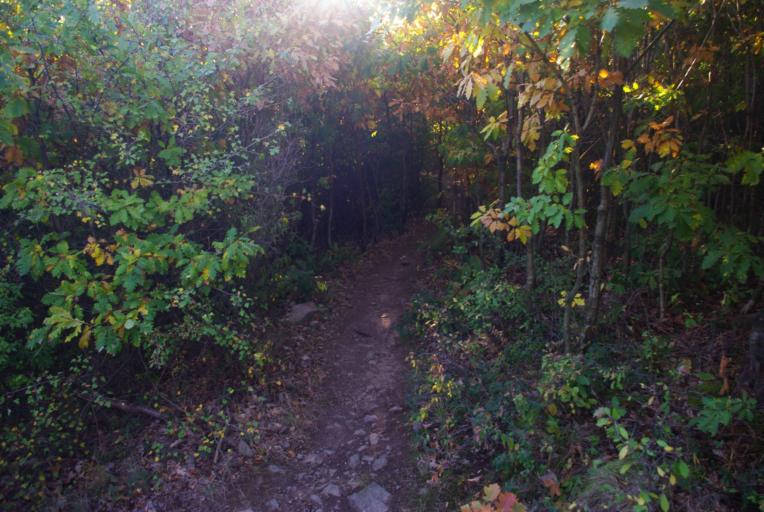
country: HU
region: Heves
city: Gyongyossolymos
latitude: 47.8361
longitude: 19.9591
